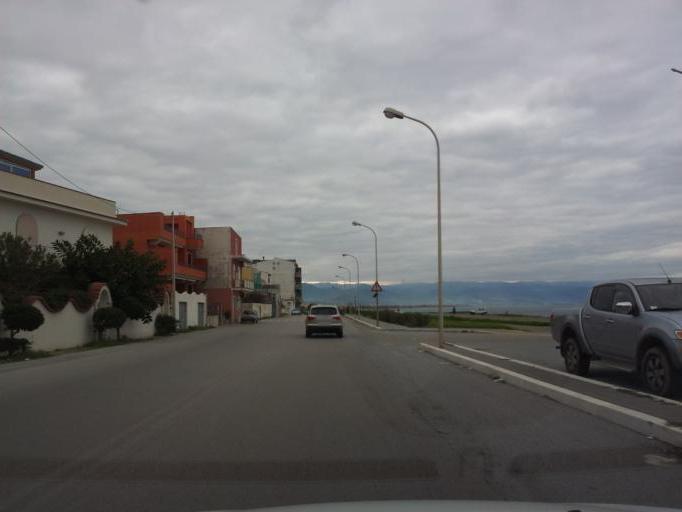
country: IT
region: Sicily
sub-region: Messina
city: Milazzo
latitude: 38.2101
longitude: 15.2290
